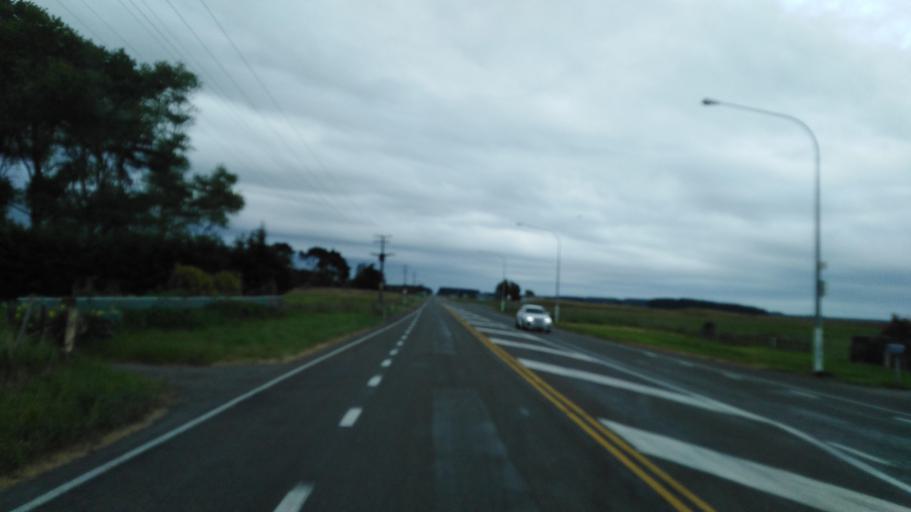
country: NZ
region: Manawatu-Wanganui
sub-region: Horowhenua District
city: Foxton
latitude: -40.3918
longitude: 175.3150
